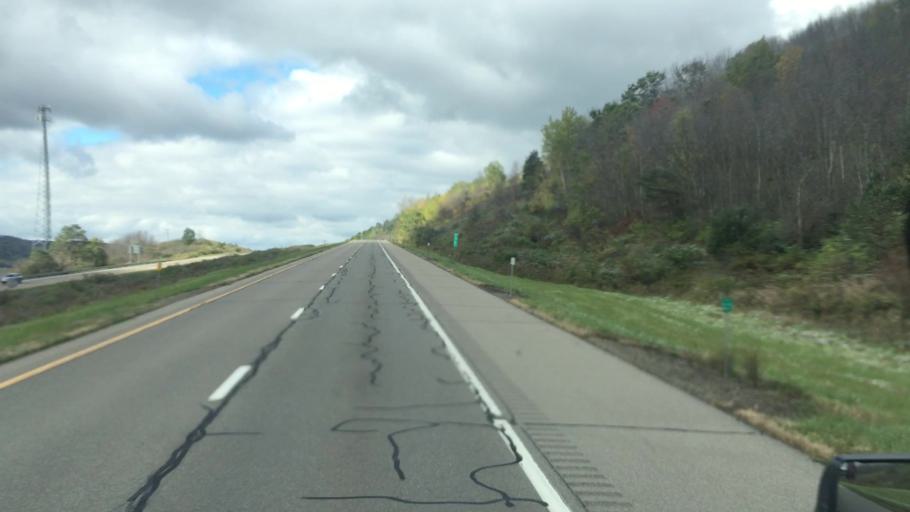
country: US
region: New York
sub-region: Allegany County
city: Friendship
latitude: 42.2091
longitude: -78.1941
